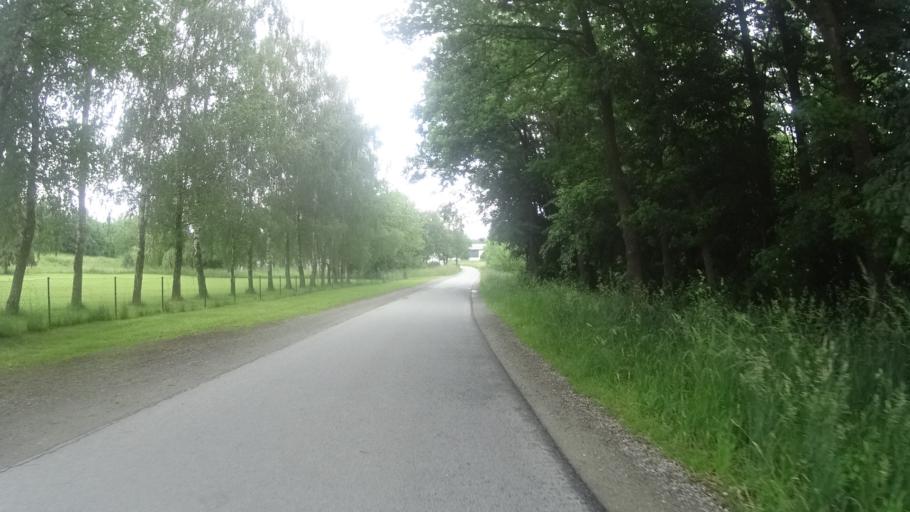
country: DE
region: Bavaria
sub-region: Lower Bavaria
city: Postmunster
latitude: 48.4247
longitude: 12.9003
